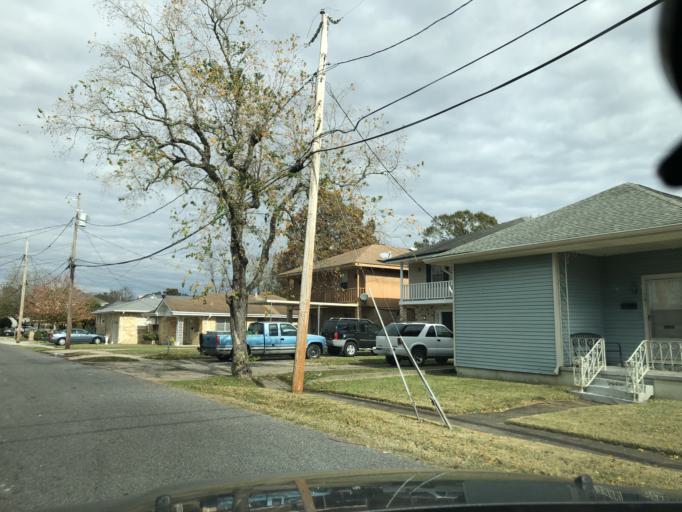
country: US
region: Louisiana
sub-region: Jefferson Parish
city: Metairie Terrace
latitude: 29.9800
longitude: -90.1644
